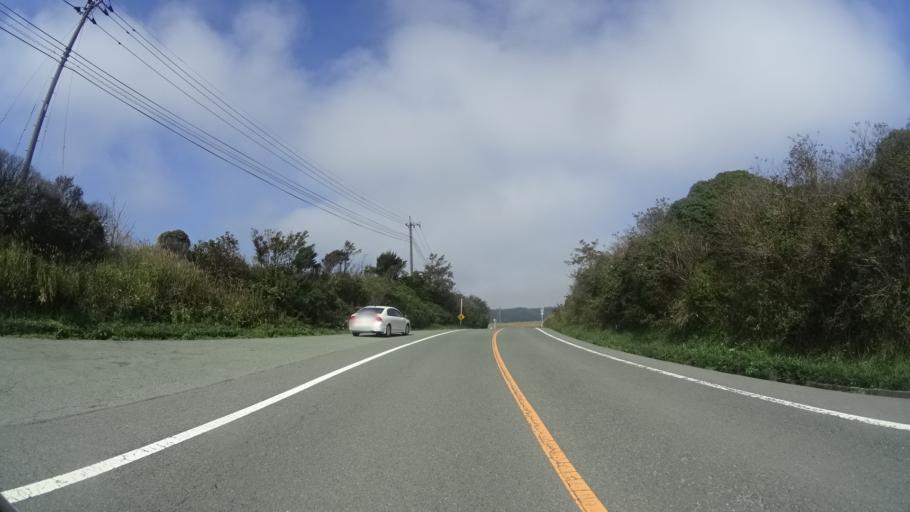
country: JP
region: Kumamoto
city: Aso
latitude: 32.9429
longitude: 130.9782
